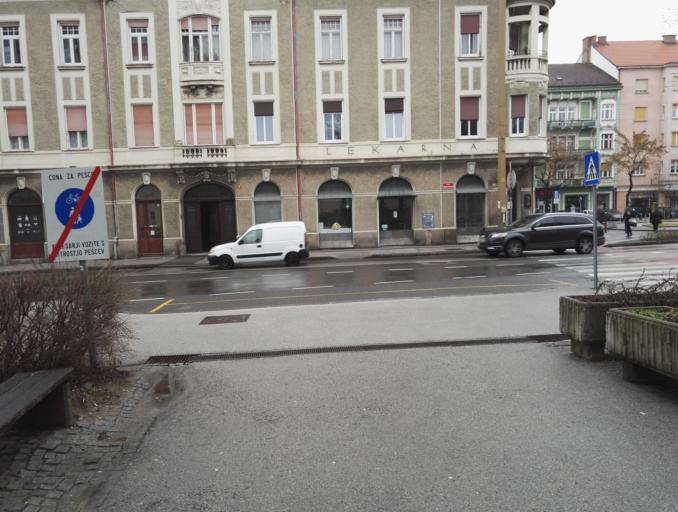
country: SI
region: Maribor
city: Maribor
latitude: 46.5578
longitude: 15.6475
